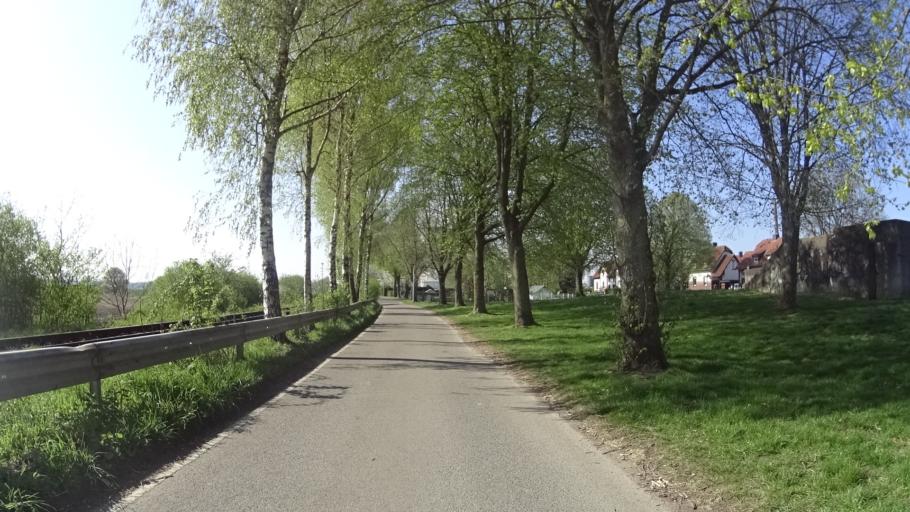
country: DE
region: North Rhine-Westphalia
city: Rheinberg
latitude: 51.5678
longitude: 6.5882
